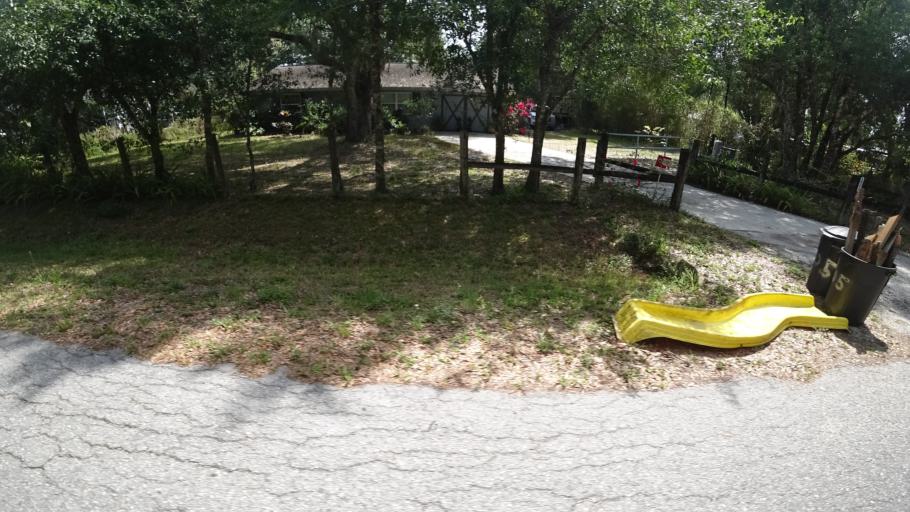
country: US
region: Florida
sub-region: Sarasota County
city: Lake Sarasota
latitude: 27.3521
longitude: -82.1636
